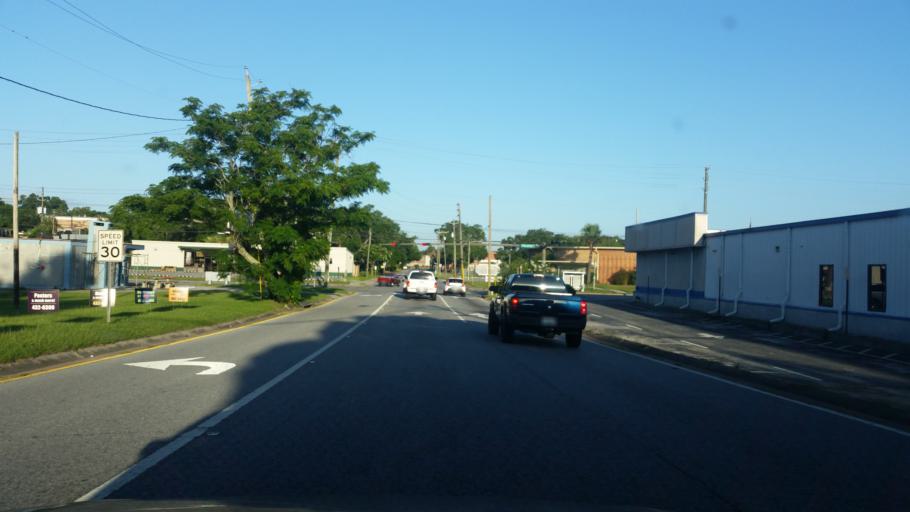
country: US
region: Florida
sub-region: Escambia County
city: Goulding
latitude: 30.4347
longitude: -87.2196
